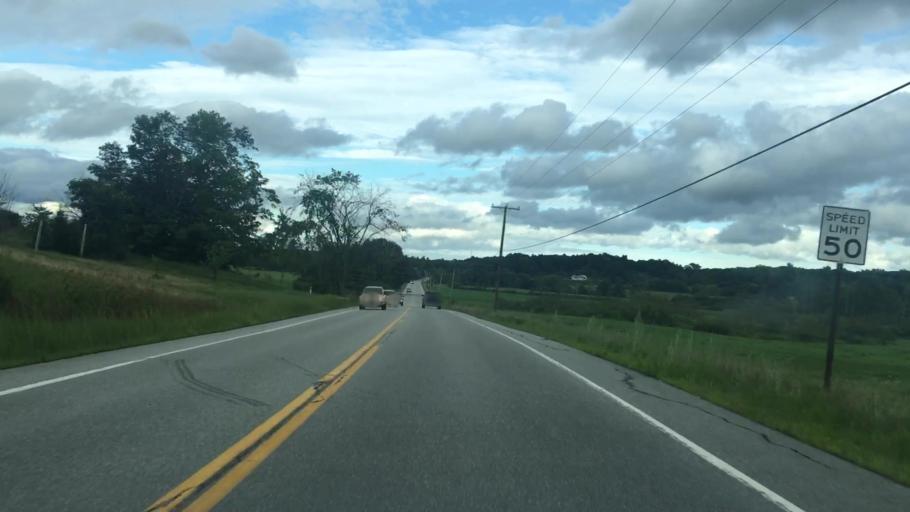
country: US
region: Maine
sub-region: York County
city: Dayton
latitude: 43.5416
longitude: -70.5579
